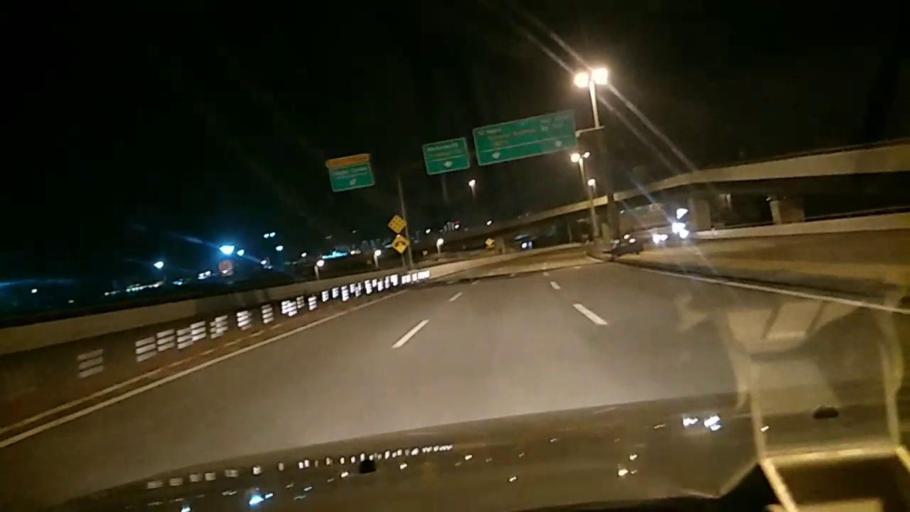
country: MY
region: Penang
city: Butterworth
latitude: 5.3910
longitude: 100.3716
